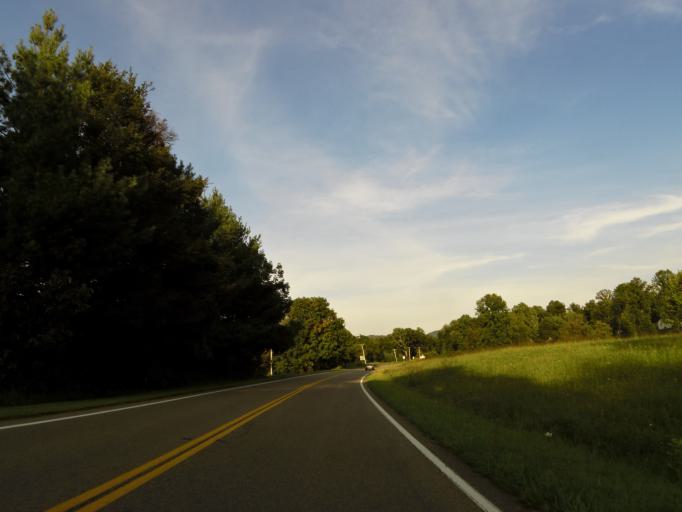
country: US
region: Virginia
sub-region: Washington County
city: Emory
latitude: 36.6418
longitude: -81.8093
